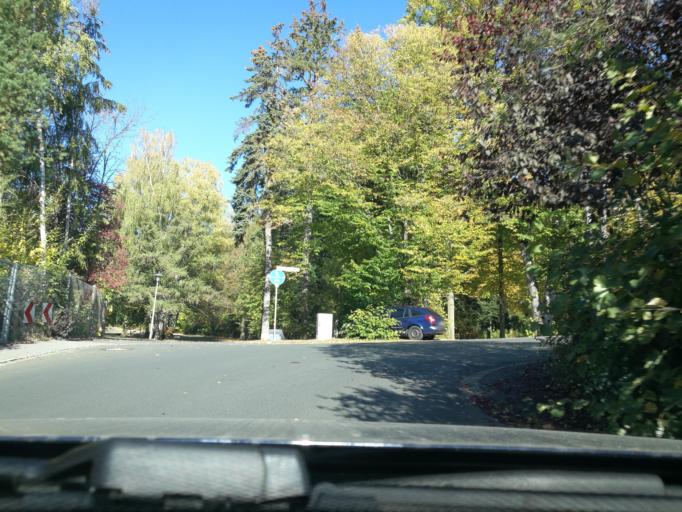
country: DE
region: Bavaria
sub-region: Regierungsbezirk Mittelfranken
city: Zirndorf
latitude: 49.4516
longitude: 10.9467
